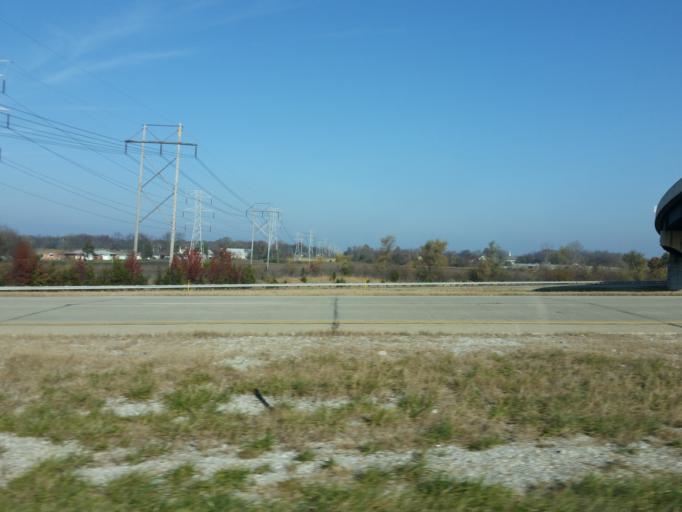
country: US
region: Indiana
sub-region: Marion County
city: Beech Grove
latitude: 39.7320
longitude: -86.0475
